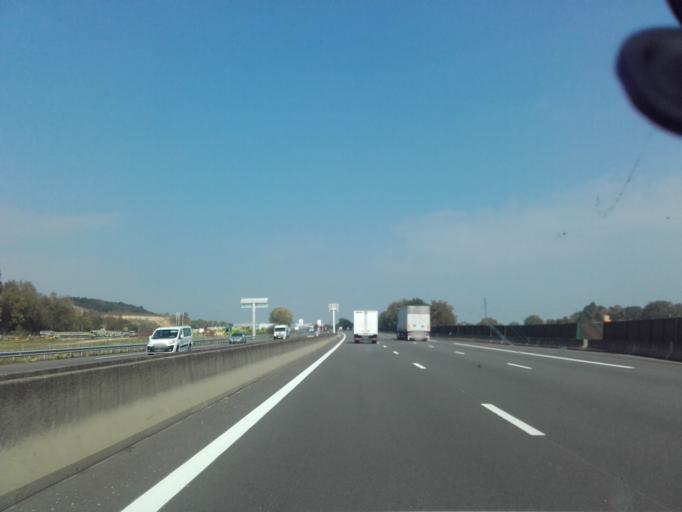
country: FR
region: Bourgogne
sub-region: Departement de Saone-et-Loire
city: Saint-Martin-Belle-Roche
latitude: 46.3799
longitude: 4.8468
